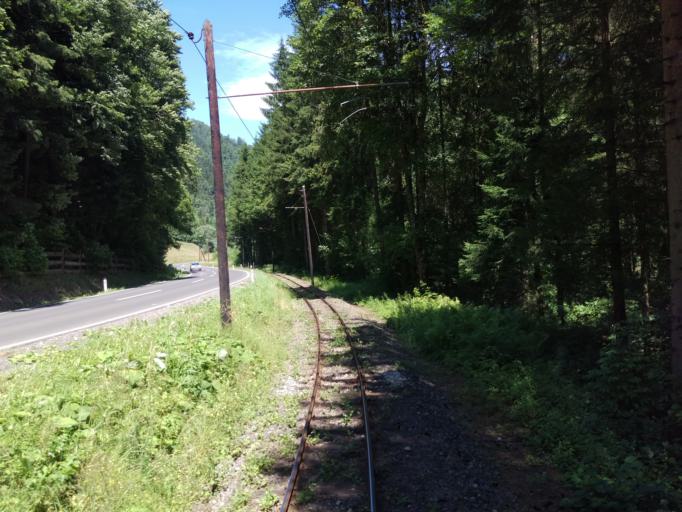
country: AT
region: Styria
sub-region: Politischer Bezirk Bruck-Muerzzuschlag
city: Pernegg an der Mur
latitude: 47.3644
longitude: 15.3791
